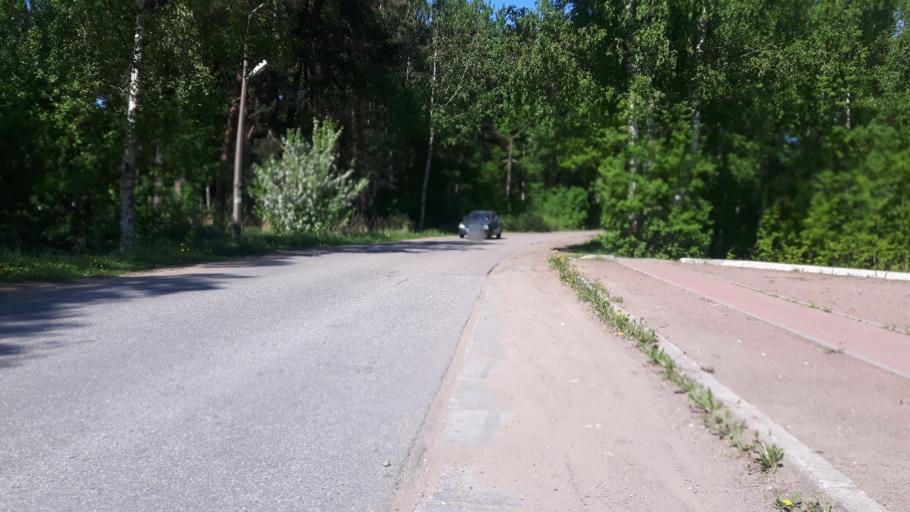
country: RU
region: Leningrad
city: Lebyazh'ye
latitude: 59.9616
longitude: 29.4145
